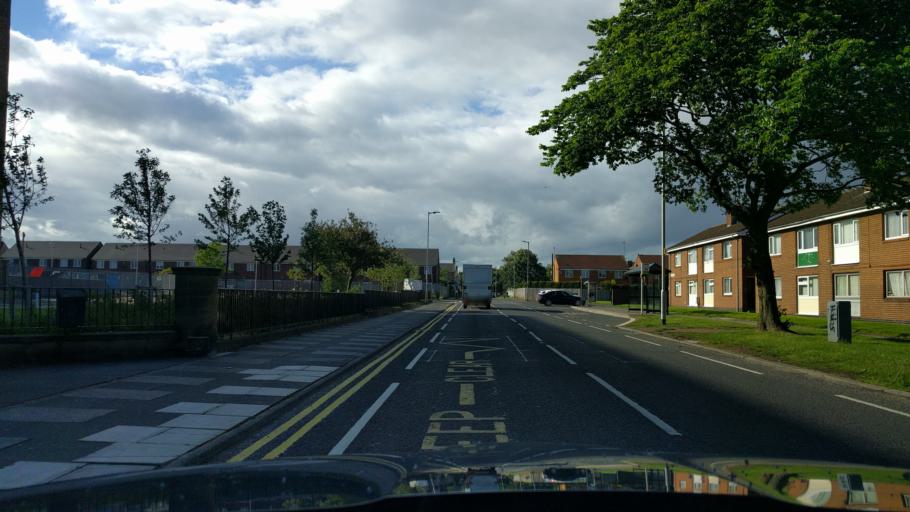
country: GB
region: England
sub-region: Northumberland
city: Ashington
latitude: 55.1734
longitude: -1.5564
